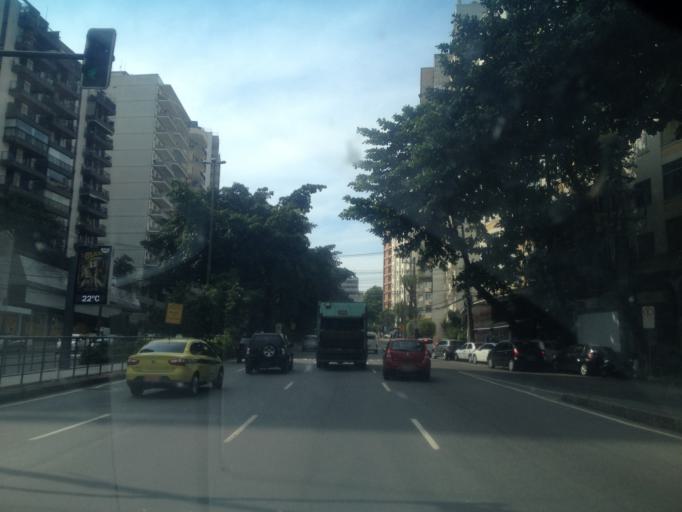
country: BR
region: Rio de Janeiro
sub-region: Rio De Janeiro
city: Rio de Janeiro
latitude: -22.9602
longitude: -43.2025
